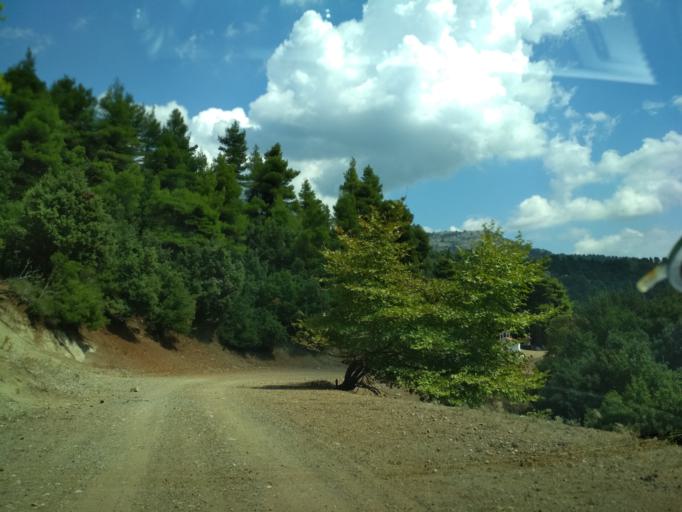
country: GR
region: Central Greece
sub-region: Nomos Evvoias
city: Roviai
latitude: 38.8457
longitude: 23.2801
